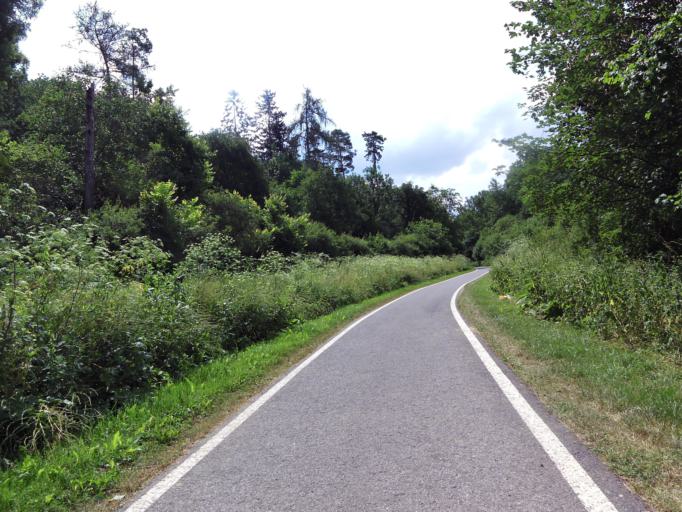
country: DE
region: Bavaria
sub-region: Regierungsbezirk Unterfranken
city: Reichenberg
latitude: 49.7439
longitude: 9.9482
